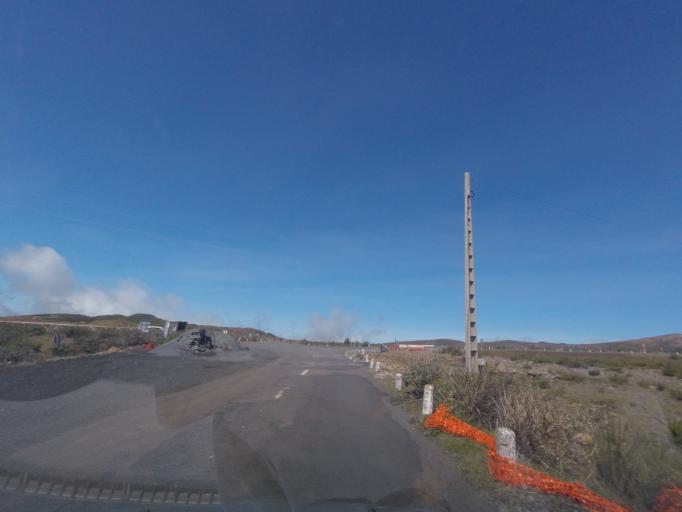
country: PT
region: Madeira
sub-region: Sao Vicente
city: Sao Vicente
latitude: 32.7573
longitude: -17.0971
